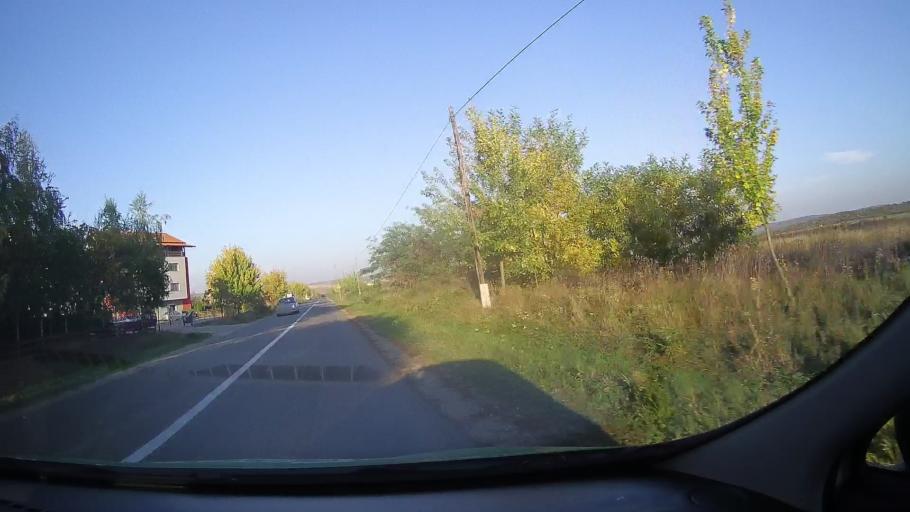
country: RO
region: Bihor
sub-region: Comuna Paleu
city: Paleu
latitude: 47.1114
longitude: 21.9368
